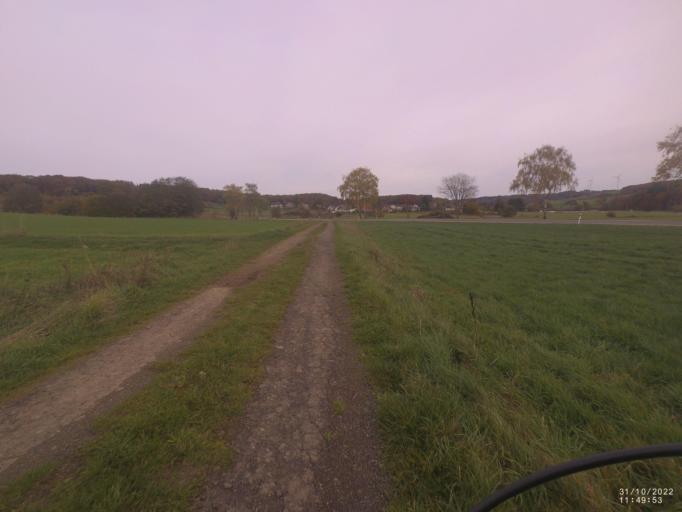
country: DE
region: Rheinland-Pfalz
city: Neichen
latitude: 50.2598
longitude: 6.8629
